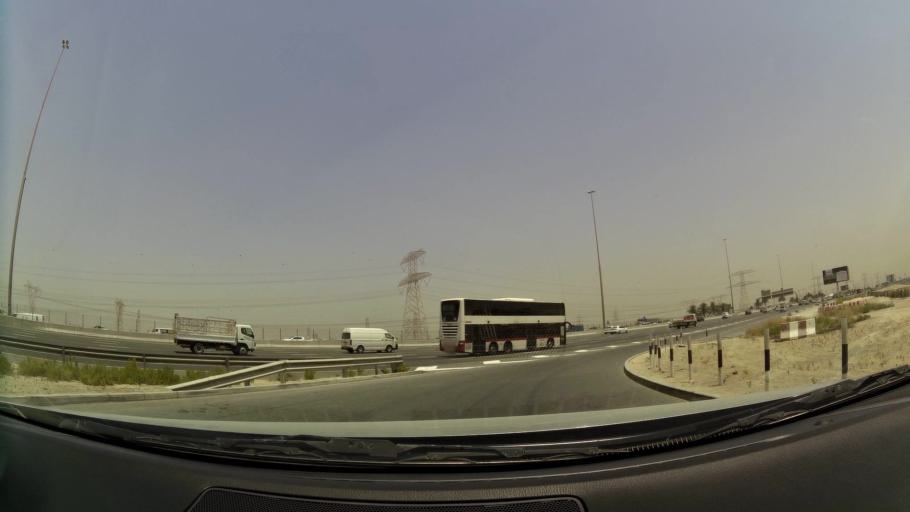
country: AE
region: Ash Shariqah
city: Sharjah
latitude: 25.1979
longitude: 55.3972
